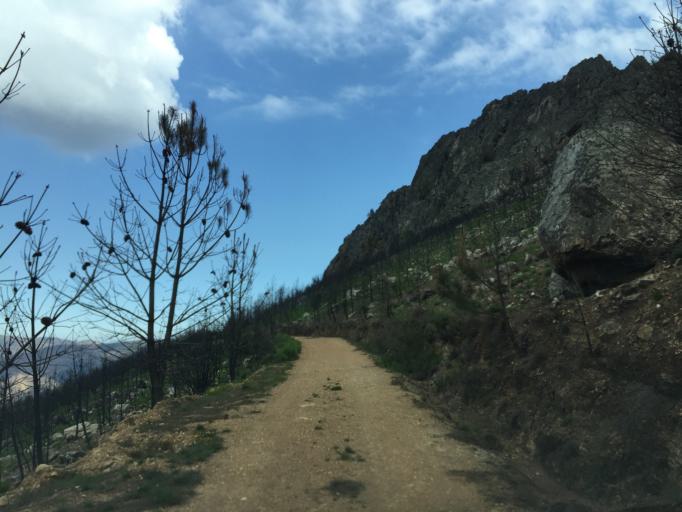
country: PT
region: Coimbra
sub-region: Pampilhosa da Serra
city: Pampilhosa da Serra
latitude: 40.1534
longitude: -7.9283
